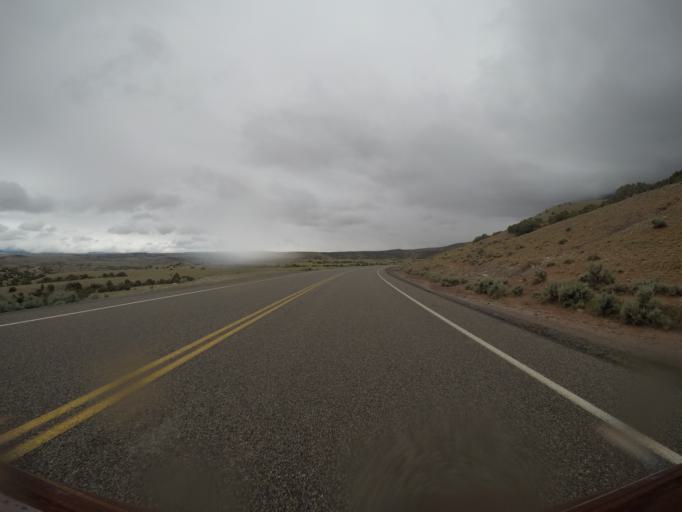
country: US
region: Wyoming
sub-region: Big Horn County
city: Lovell
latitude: 45.0709
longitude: -108.2548
